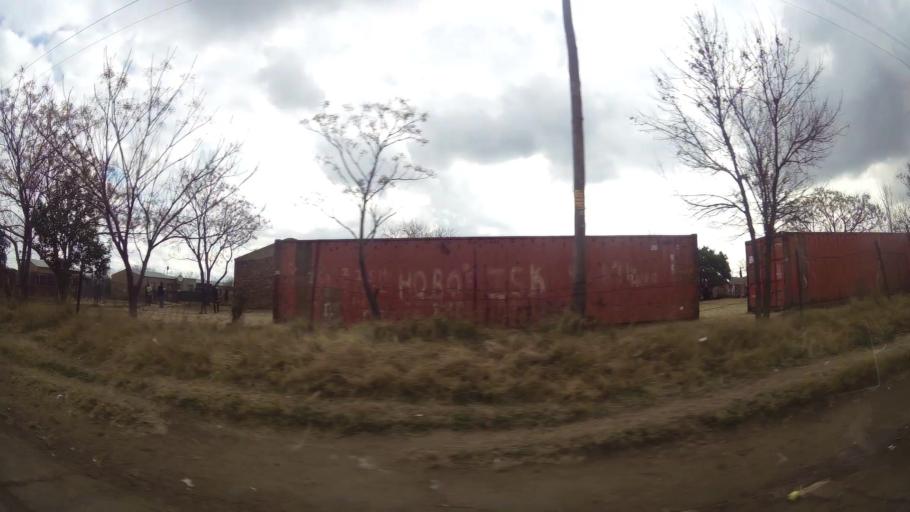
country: ZA
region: Orange Free State
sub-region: Fezile Dabi District Municipality
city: Sasolburg
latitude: -26.8564
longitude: 27.8580
